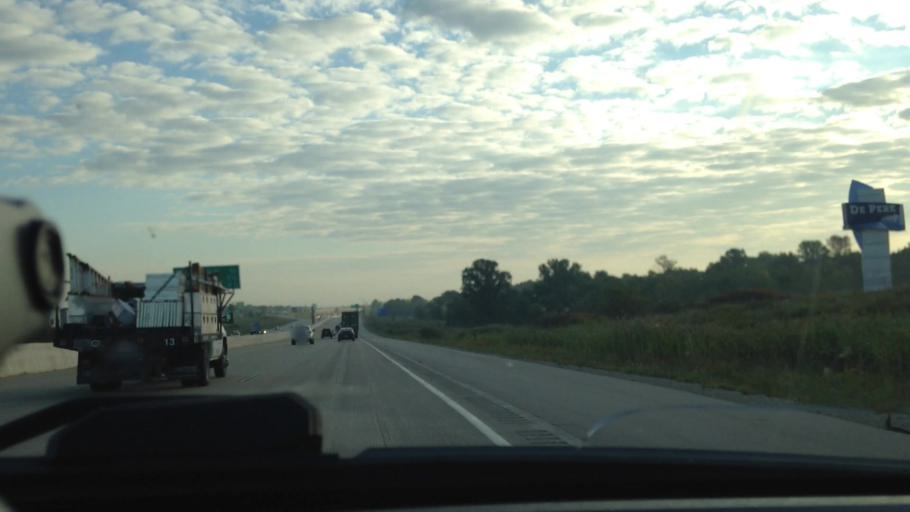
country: US
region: Wisconsin
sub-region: Brown County
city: De Pere
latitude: 44.4235
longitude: -88.1228
